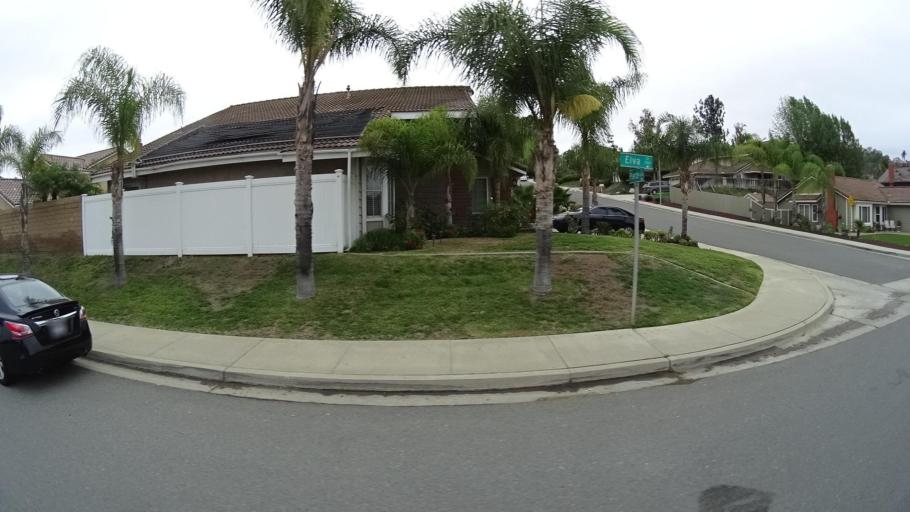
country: US
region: California
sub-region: San Diego County
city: Rancho San Diego
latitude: 32.7580
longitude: -116.9107
